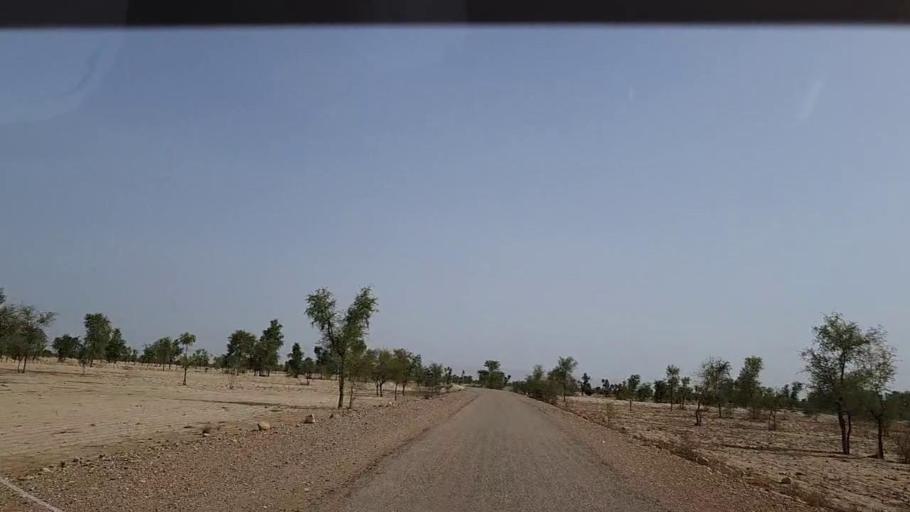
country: PK
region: Sindh
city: Johi
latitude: 26.6322
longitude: 67.5014
